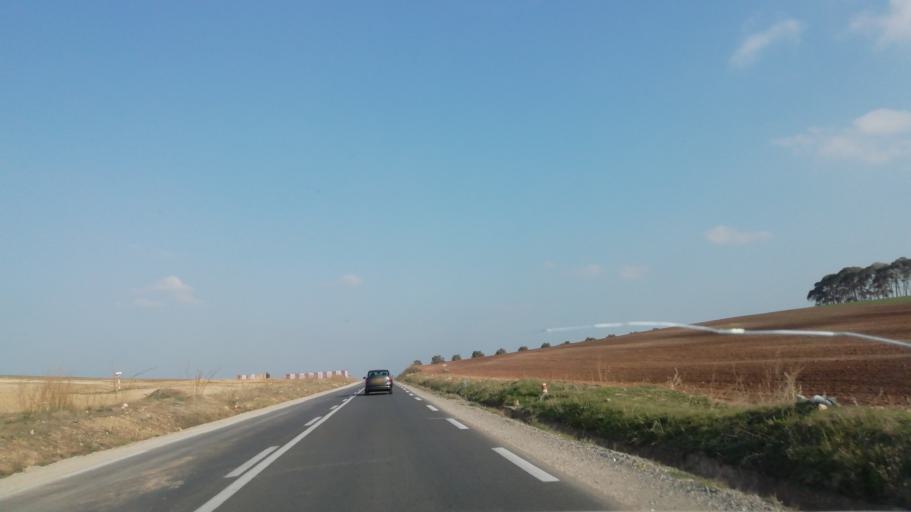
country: DZ
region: Ain Temouchent
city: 'Ain Temouchent
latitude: 35.3041
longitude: -1.0651
